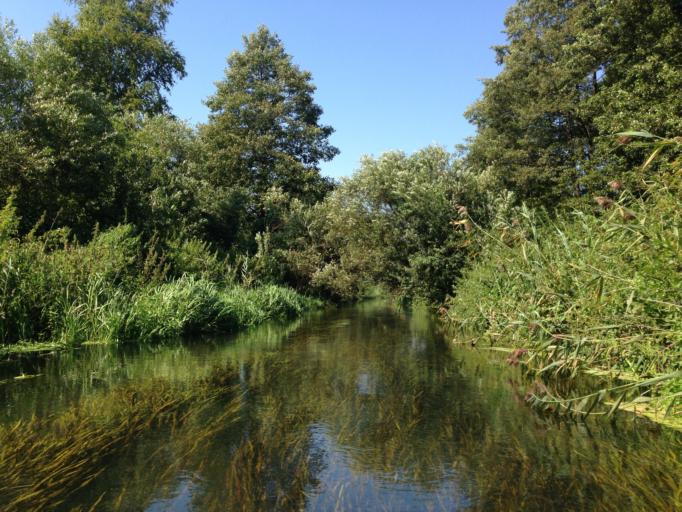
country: PL
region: Kujawsko-Pomorskie
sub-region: Powiat brodnicki
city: Bartniczka
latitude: 53.2815
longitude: 19.5759
